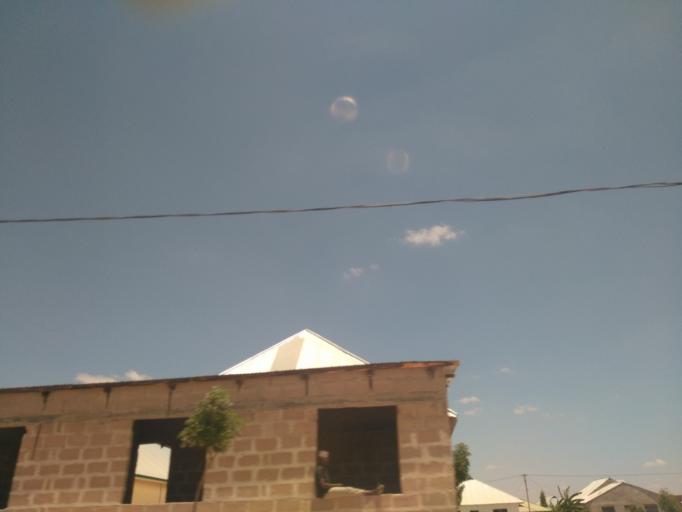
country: TZ
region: Dodoma
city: Dodoma
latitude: -6.1464
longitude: 35.7351
